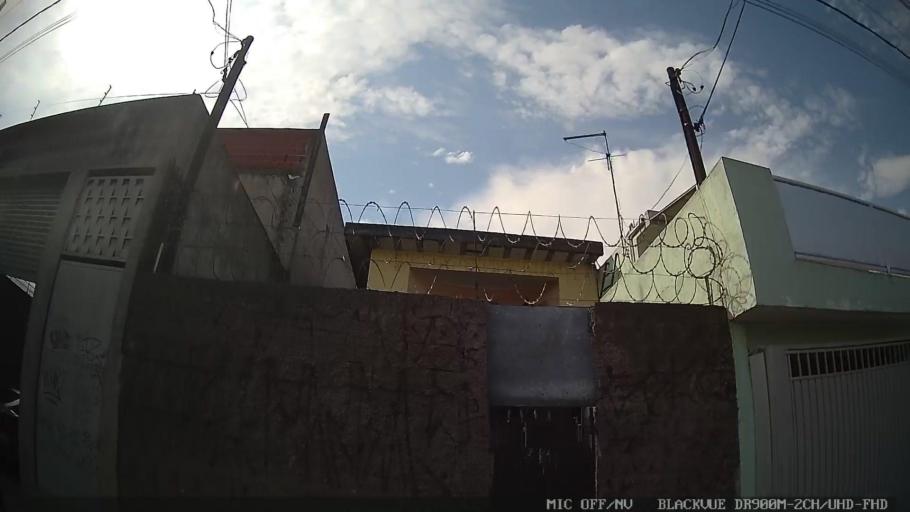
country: BR
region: Sao Paulo
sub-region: Ferraz De Vasconcelos
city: Ferraz de Vasconcelos
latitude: -23.5374
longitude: -46.4057
